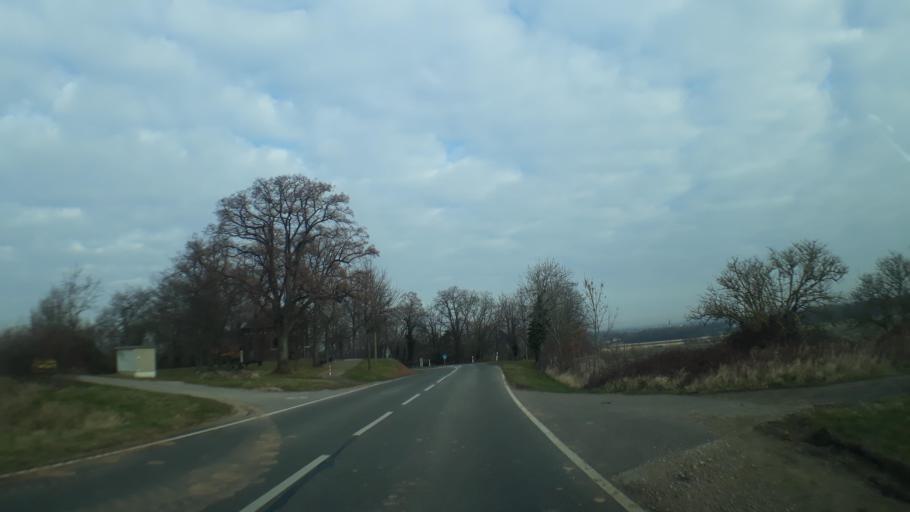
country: DE
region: North Rhine-Westphalia
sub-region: Regierungsbezirk Koln
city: Euskirchen
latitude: 50.6276
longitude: 6.7806
